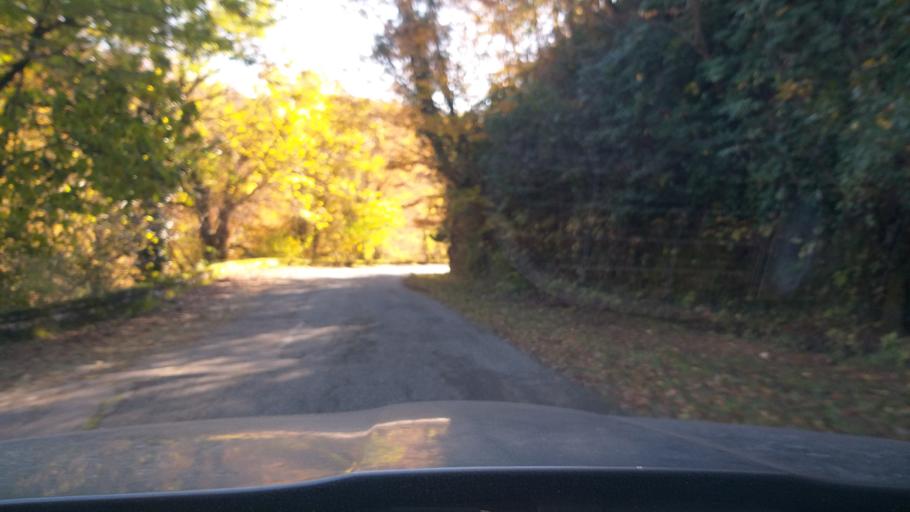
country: GE
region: Abkhazia
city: Bich'vinta
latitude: 43.1946
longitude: 40.4562
